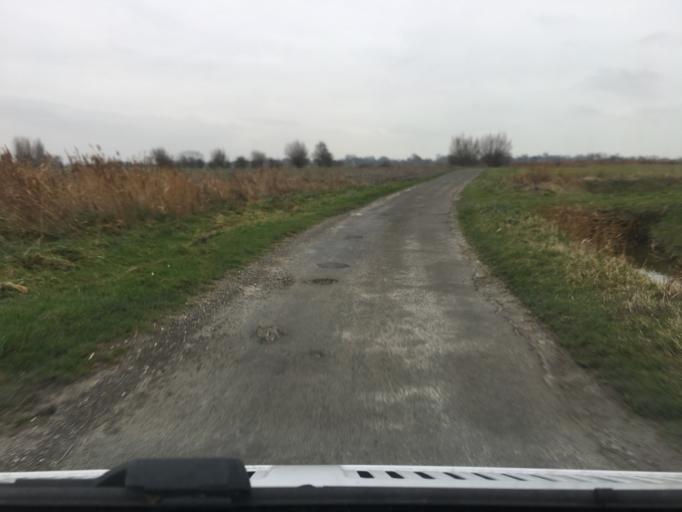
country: FR
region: Picardie
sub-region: Departement de la Somme
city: Pende
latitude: 50.1797
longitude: 1.5445
